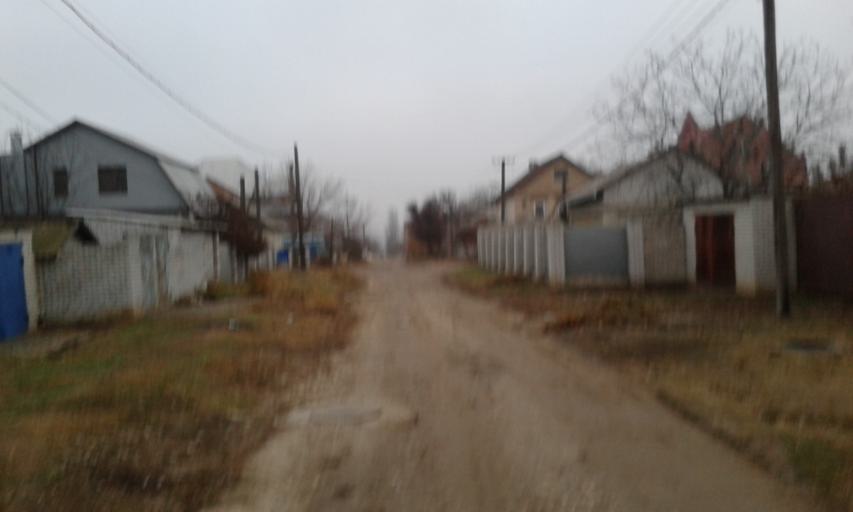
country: RU
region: Volgograd
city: Gorodishche
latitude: 48.7642
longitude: 44.4870
